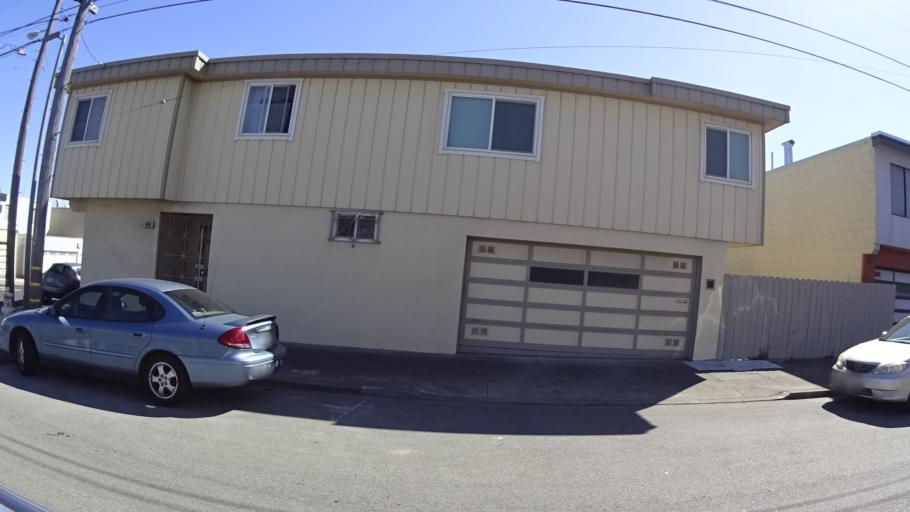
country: US
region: California
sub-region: San Francisco County
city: San Francisco
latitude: 37.7281
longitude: -122.4170
